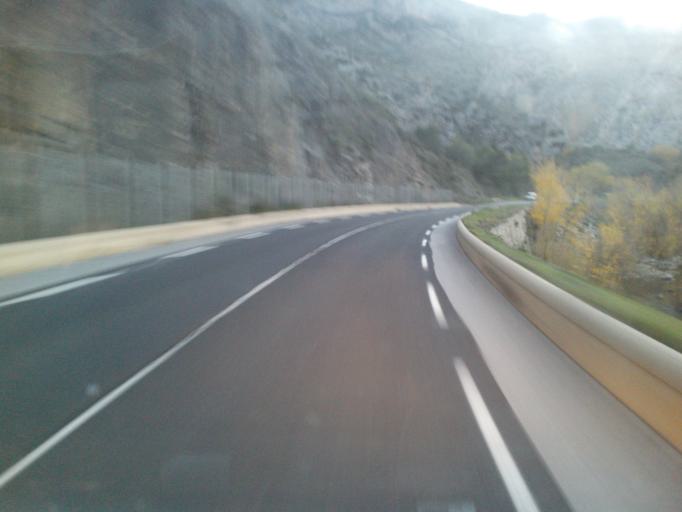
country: FR
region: Languedoc-Roussillon
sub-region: Departement des Pyrenees-Orientales
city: Baixas
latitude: 42.7733
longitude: 2.7862
